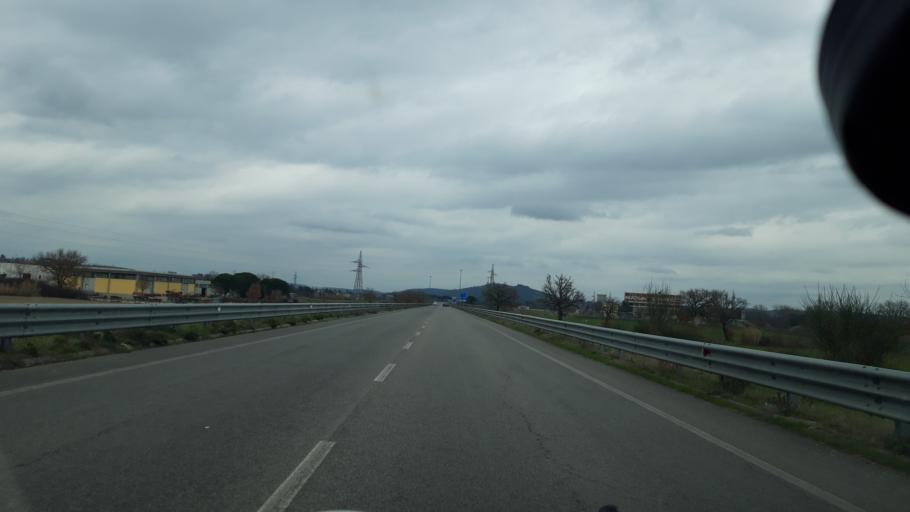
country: IT
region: Umbria
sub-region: Provincia di Perugia
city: Tavernelle
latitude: 43.0035
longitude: 12.1709
